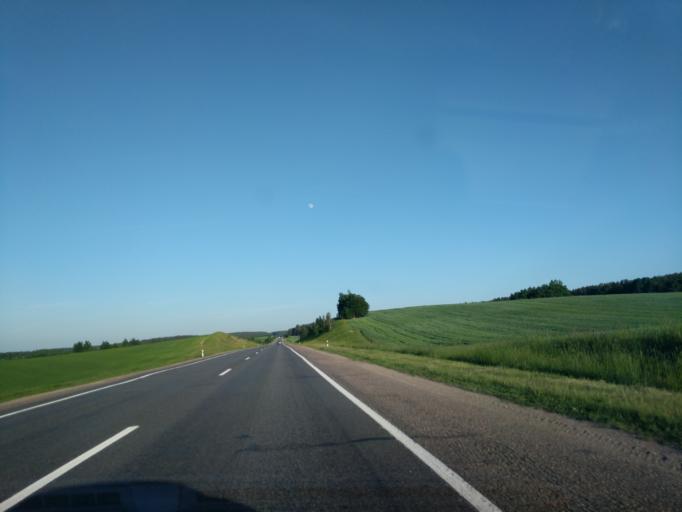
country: BY
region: Grodnenskaya
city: Kreva
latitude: 54.1953
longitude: 26.3786
